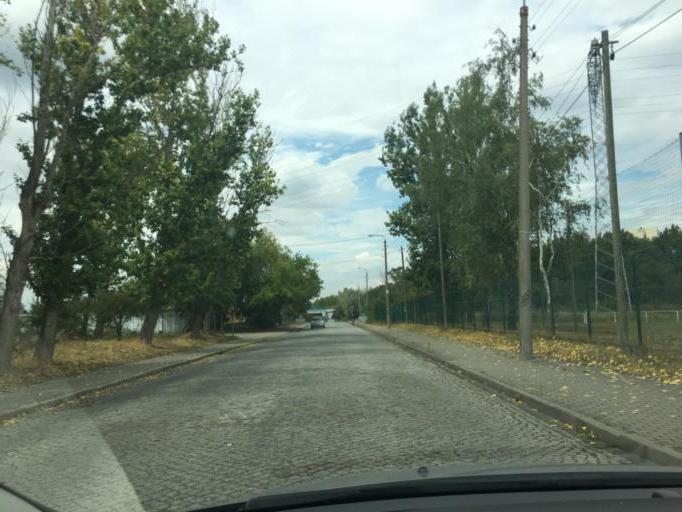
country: DE
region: Saxony-Anhalt
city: Angersdorf
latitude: 51.4475
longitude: 11.9436
